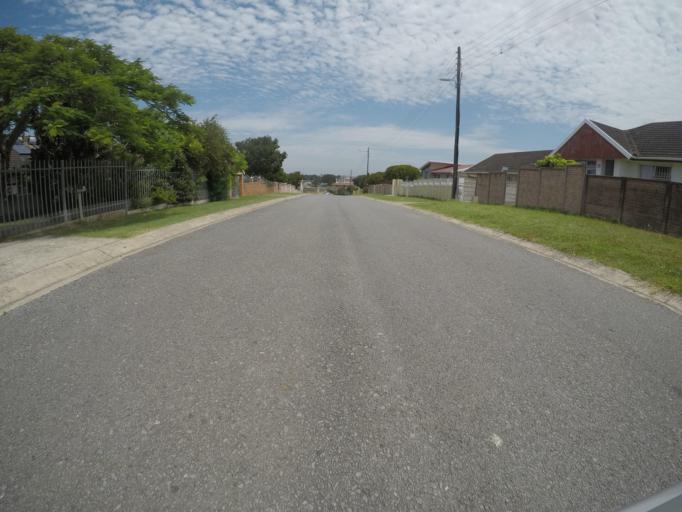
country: ZA
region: Eastern Cape
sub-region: Buffalo City Metropolitan Municipality
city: East London
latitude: -32.9844
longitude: 27.8661
